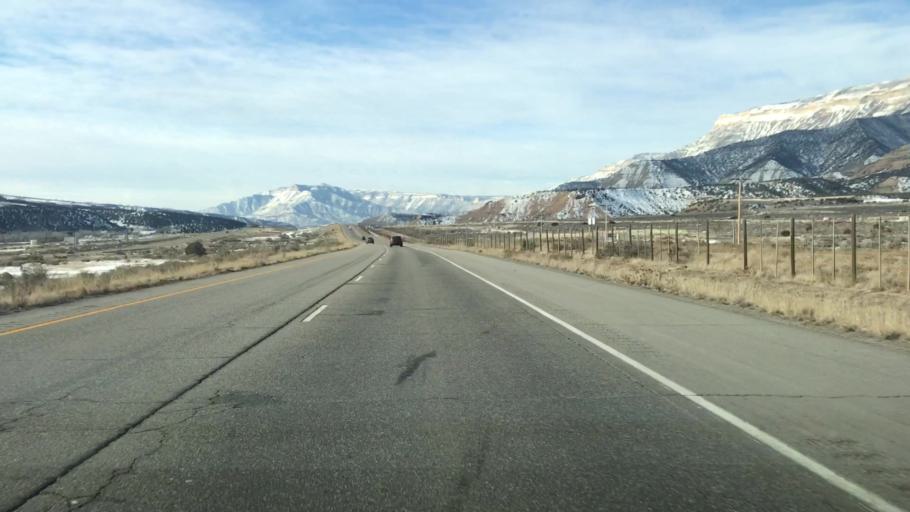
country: US
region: Colorado
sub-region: Garfield County
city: Rifle
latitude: 39.5045
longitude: -107.8980
